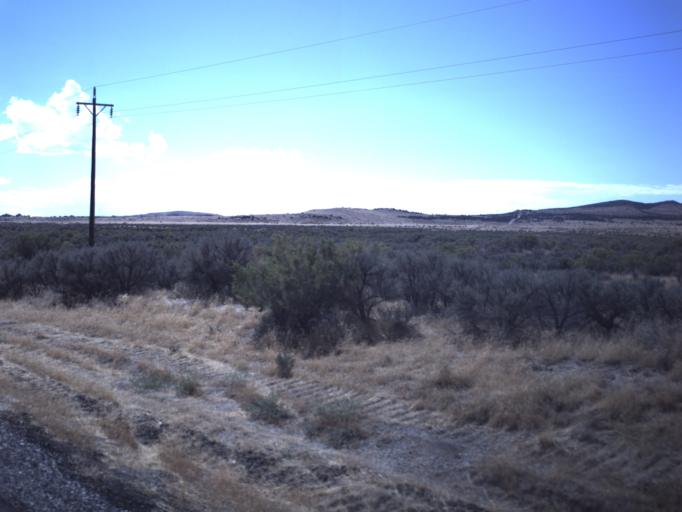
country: US
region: Utah
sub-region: Tooele County
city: Grantsville
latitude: 40.2451
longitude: -112.7092
